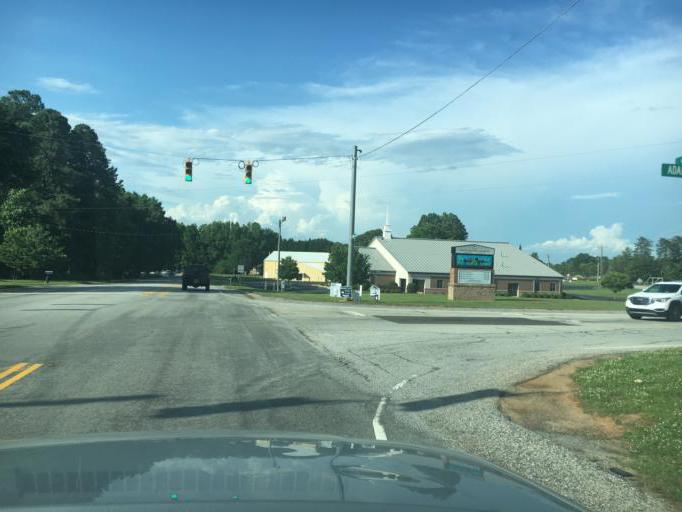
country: US
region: South Carolina
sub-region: Greenville County
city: Simpsonville
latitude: 34.7743
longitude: -82.2565
